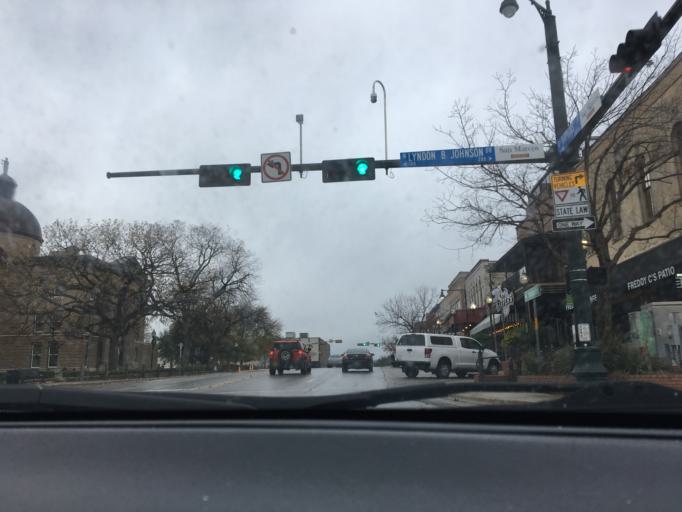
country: US
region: Texas
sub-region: Hays County
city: San Marcos
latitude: 29.8833
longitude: -97.9401
